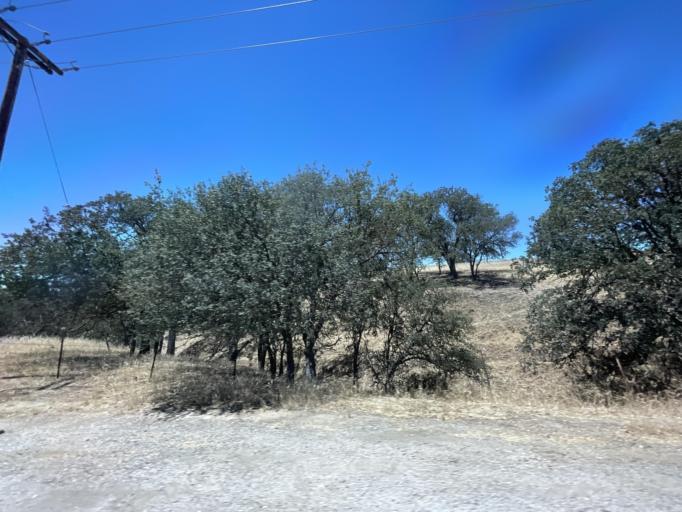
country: US
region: California
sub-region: San Luis Obispo County
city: Paso Robles
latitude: 35.6410
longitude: -120.5797
